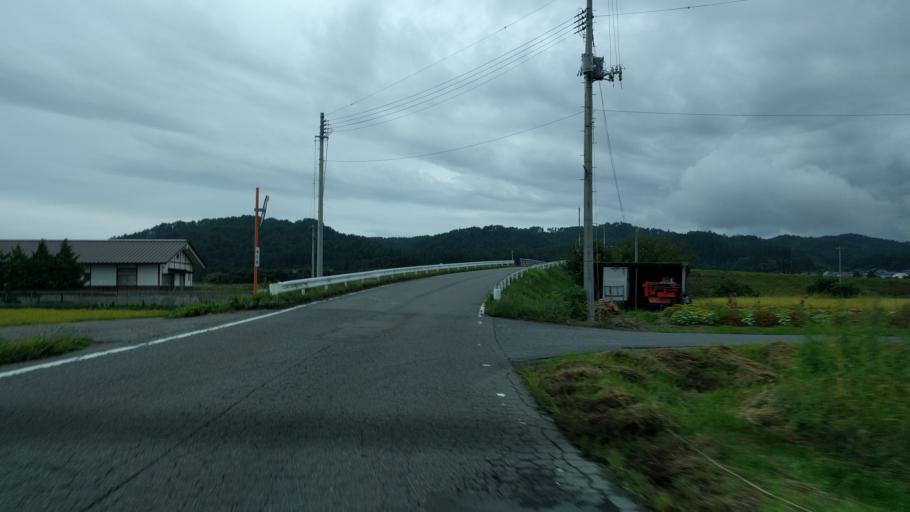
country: JP
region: Fukushima
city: Kitakata
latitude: 37.6122
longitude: 139.8381
